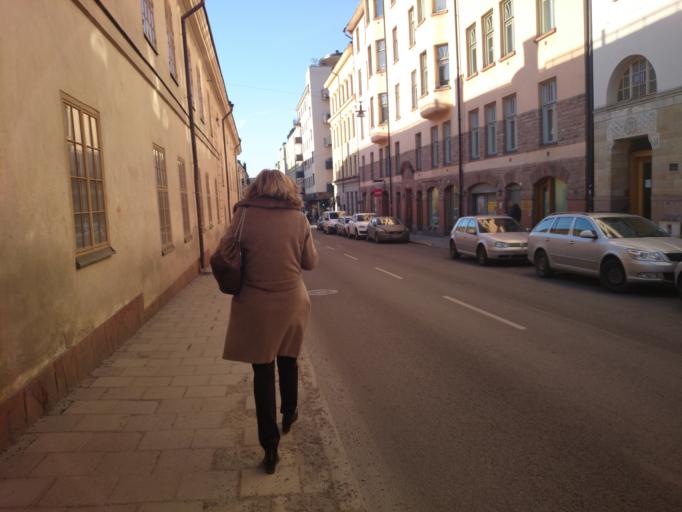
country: SE
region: Stockholm
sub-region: Stockholms Kommun
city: OEstermalm
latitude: 59.3348
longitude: 18.0786
